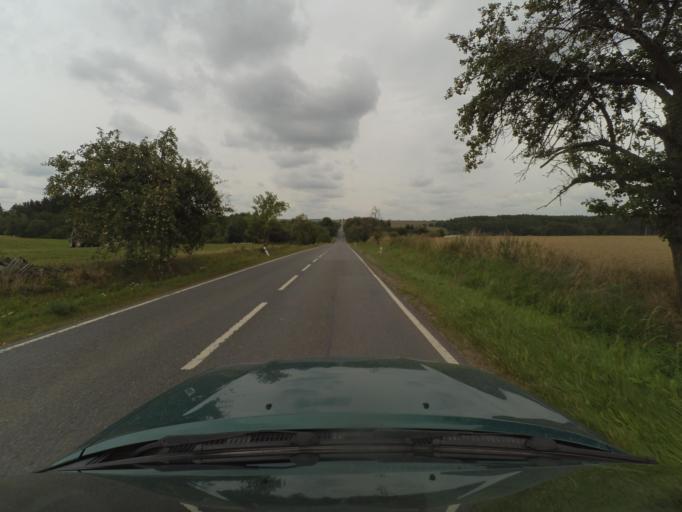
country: CZ
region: Plzensky
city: Kozlany
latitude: 50.0298
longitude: 13.5839
